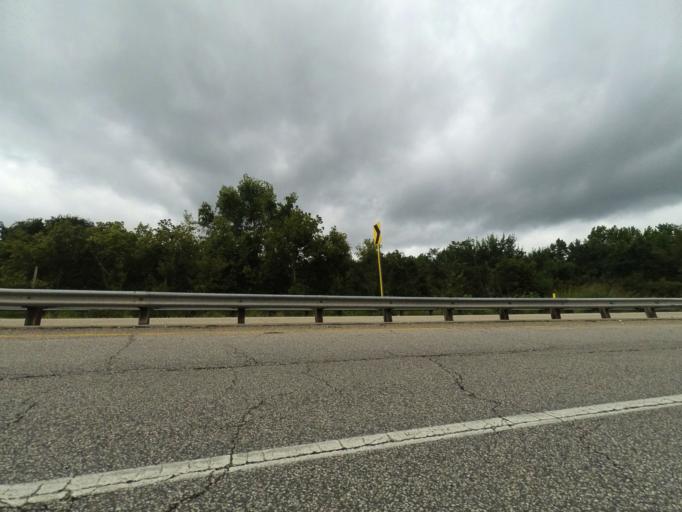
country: US
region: West Virginia
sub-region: Cabell County
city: Huntington
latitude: 38.4353
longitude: -82.4591
